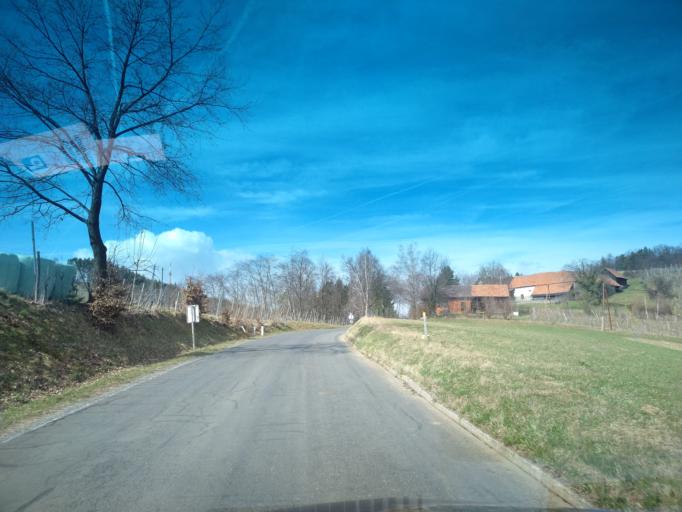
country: AT
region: Styria
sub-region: Politischer Bezirk Leibnitz
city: Sankt Nikolai im Sausal
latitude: 46.7975
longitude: 15.4320
